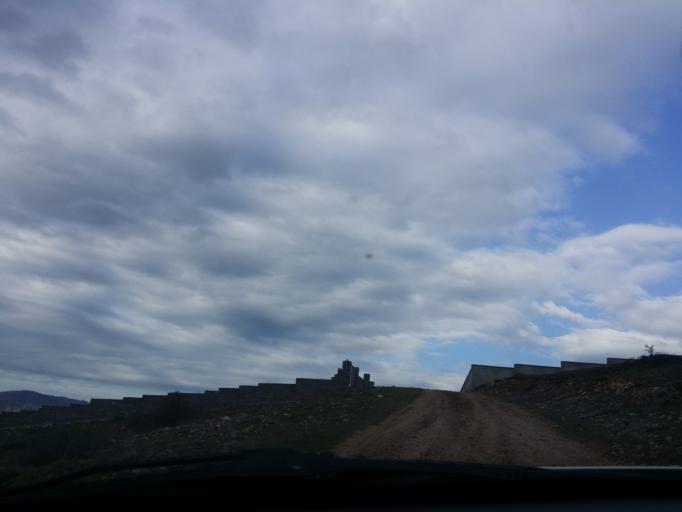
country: IR
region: Mazandaran
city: `Abbasabad
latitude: 36.4999
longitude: 51.1795
